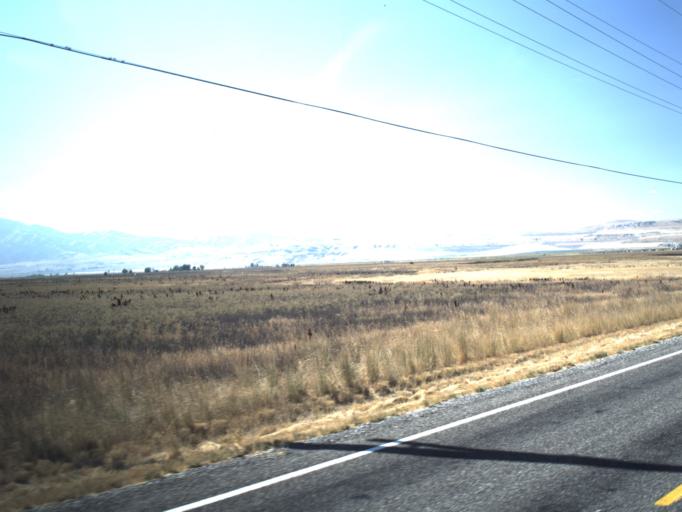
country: US
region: Utah
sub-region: Cache County
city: Benson
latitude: 41.8450
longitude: -111.9248
